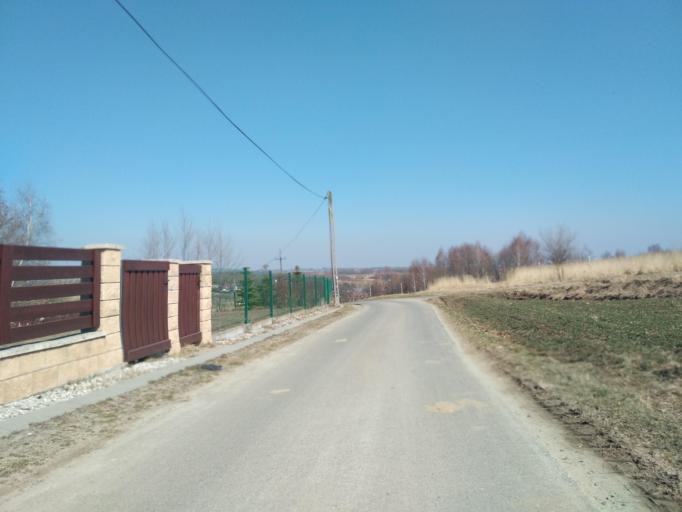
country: PL
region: Subcarpathian Voivodeship
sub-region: Powiat rzeszowski
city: Niechobrz
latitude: 49.9720
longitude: 21.8770
